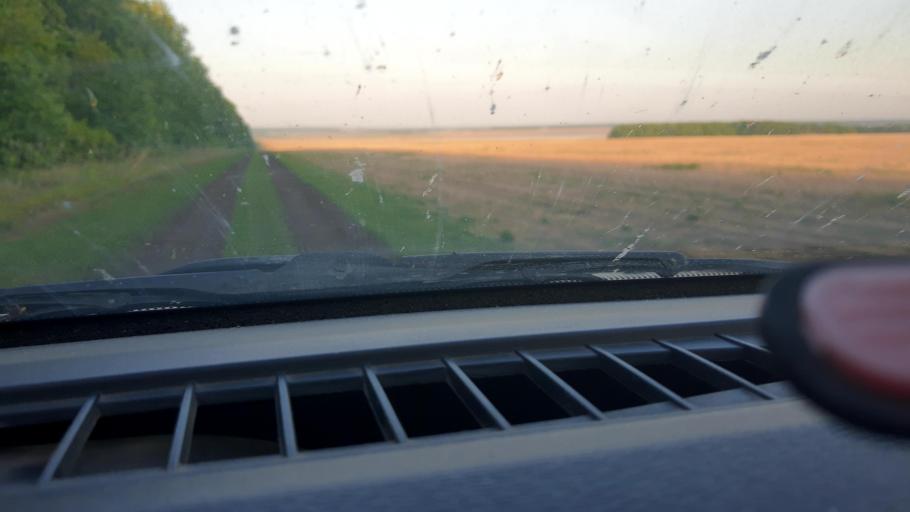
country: RU
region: Bashkortostan
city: Asanovo
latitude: 54.8705
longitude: 55.5337
